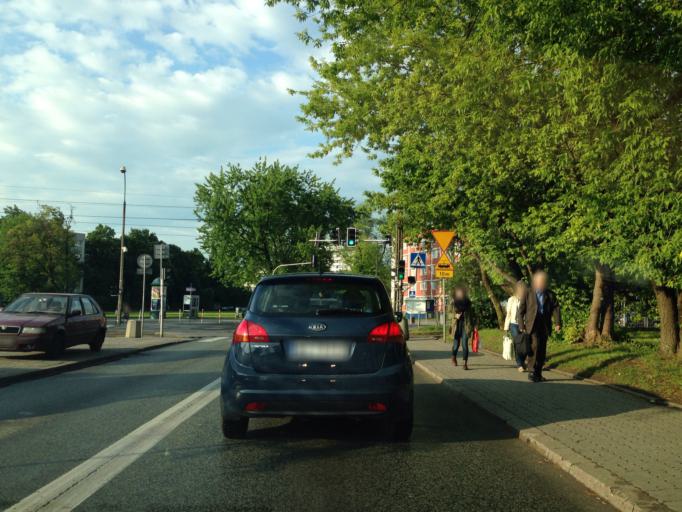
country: PL
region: Masovian Voivodeship
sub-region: Warszawa
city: Zoliborz
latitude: 52.2640
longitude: 20.9714
